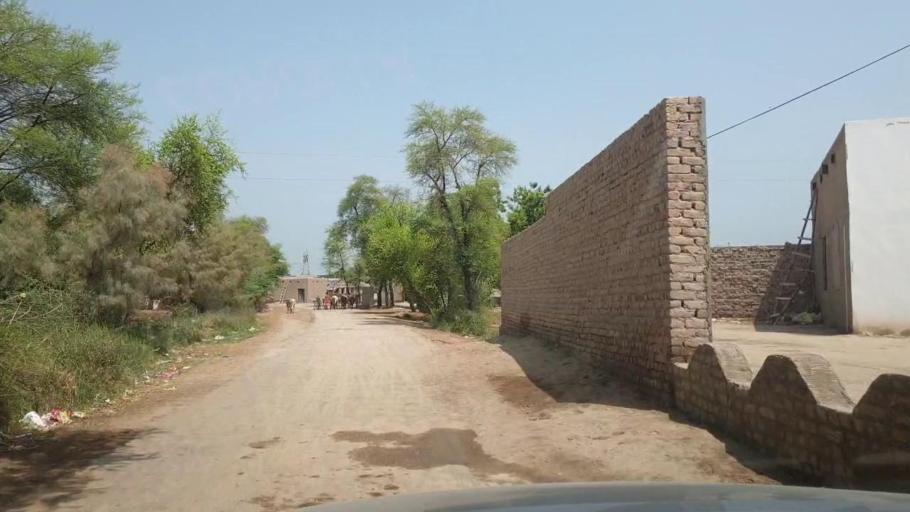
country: PK
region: Sindh
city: Madeji
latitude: 27.8086
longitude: 68.5199
